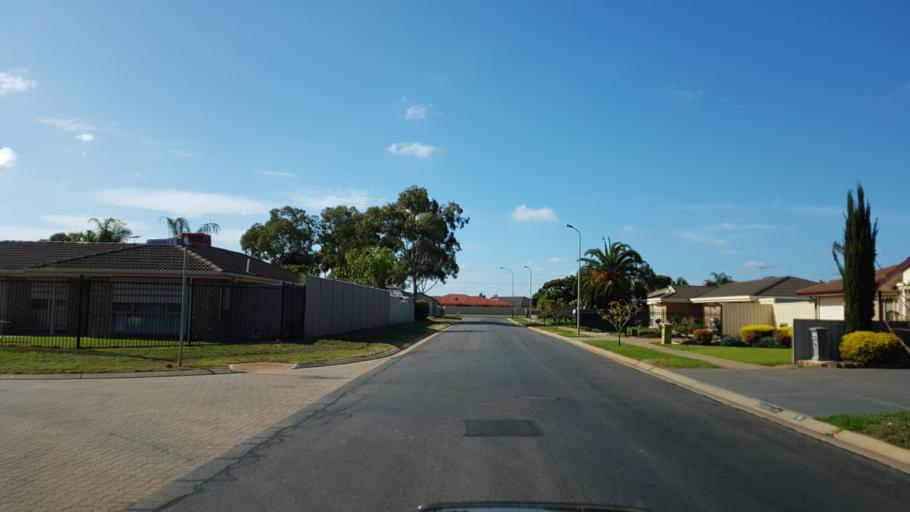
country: AU
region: South Australia
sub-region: Salisbury
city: Salisbury
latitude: -34.7349
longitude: 138.6152
